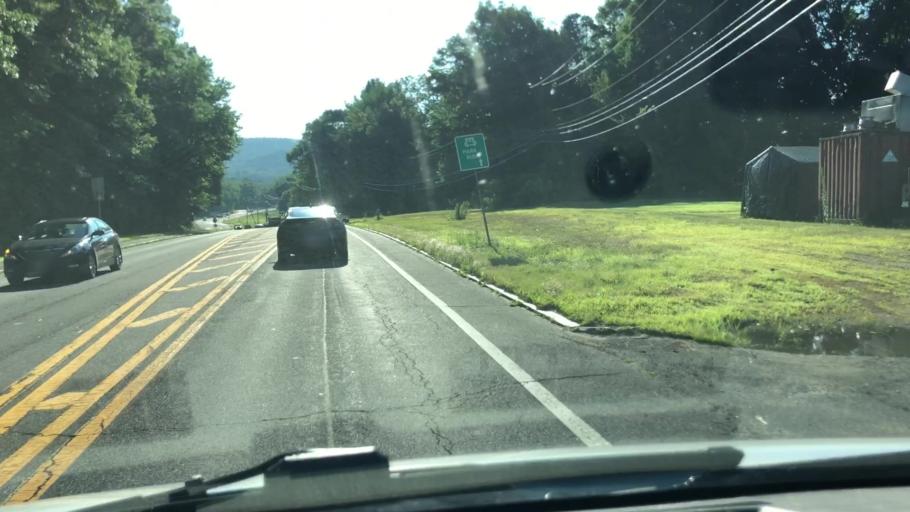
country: US
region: Massachusetts
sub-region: Franklin County
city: South Deerfield
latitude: 42.4674
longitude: -72.5937
